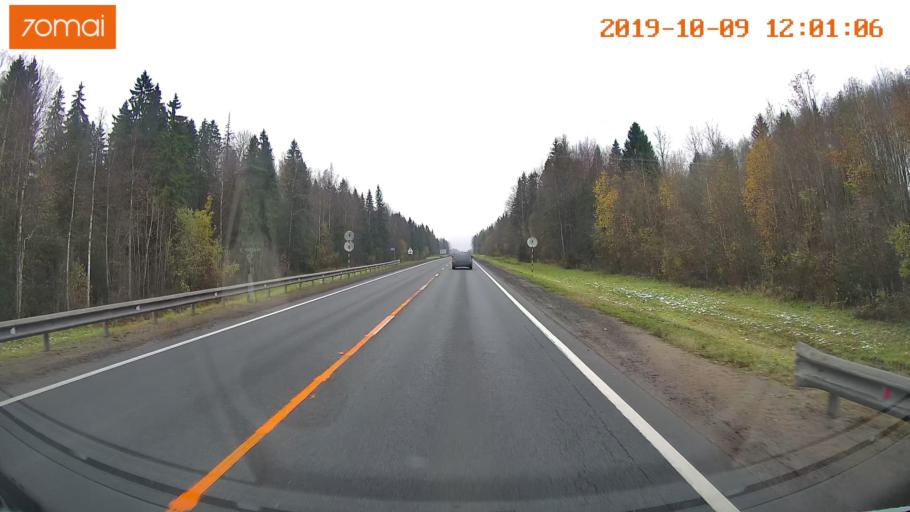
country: RU
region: Vologda
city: Gryazovets
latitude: 58.6919
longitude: 40.3018
